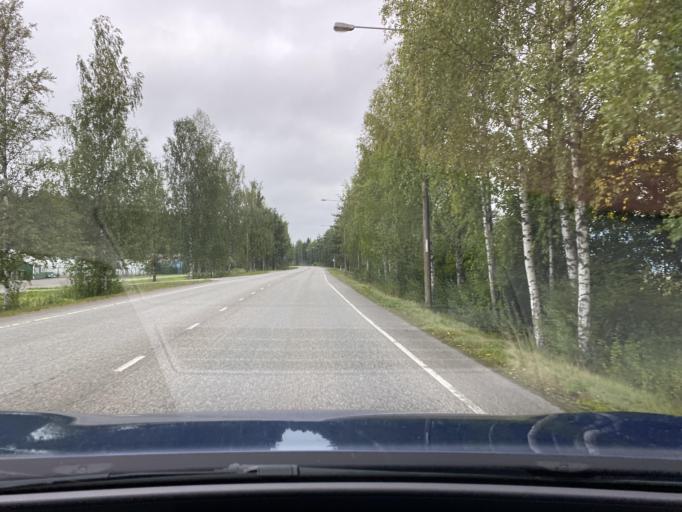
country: FI
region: Kymenlaakso
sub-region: Kouvola
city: Kouvola
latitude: 60.9002
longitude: 26.6066
